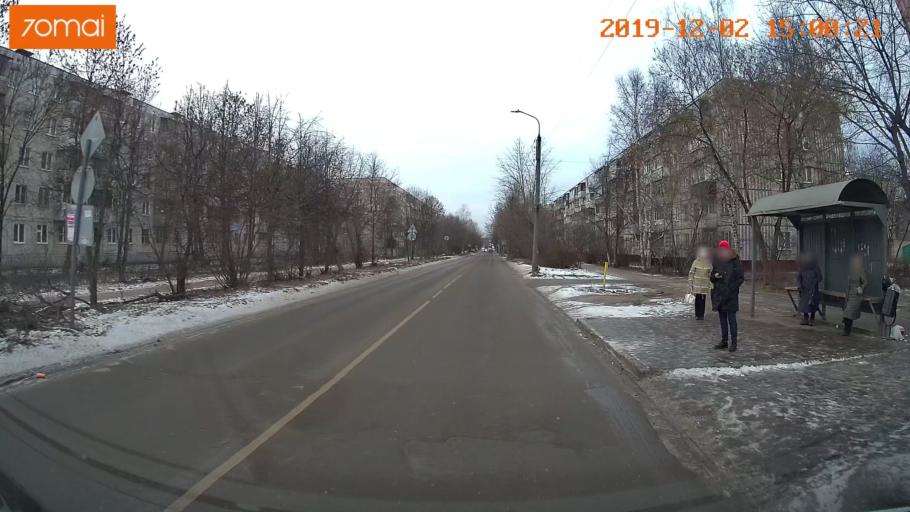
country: RU
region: Ivanovo
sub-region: Gorod Ivanovo
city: Ivanovo
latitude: 56.9699
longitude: 41.0043
